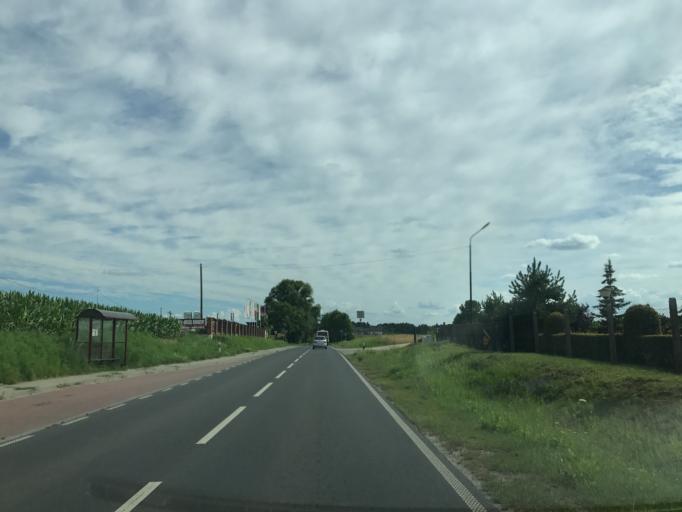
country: PL
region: Kujawsko-Pomorskie
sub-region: Powiat rypinski
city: Rypin
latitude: 53.1171
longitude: 19.3858
